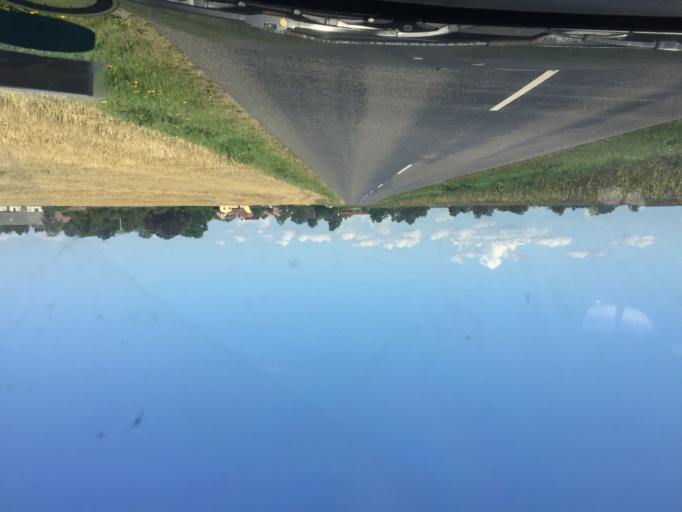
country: DK
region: Zealand
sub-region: Lolland Kommune
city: Maribo
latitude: 54.7961
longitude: 11.5303
